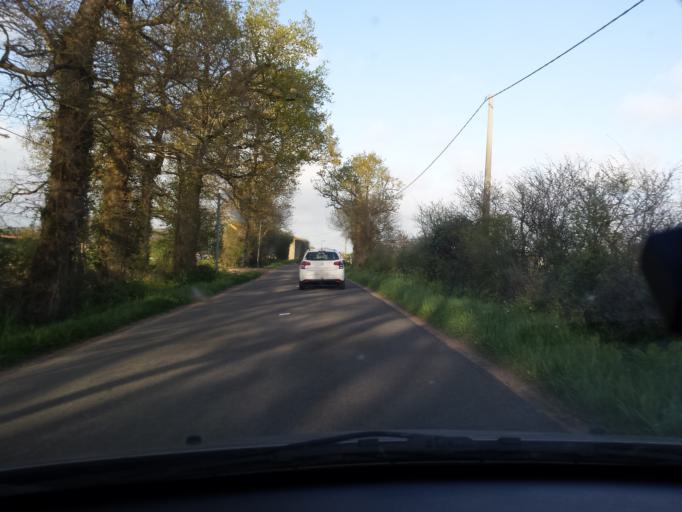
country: FR
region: Pays de la Loire
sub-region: Departement de la Vendee
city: Vaire
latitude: 46.5692
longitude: -1.7492
